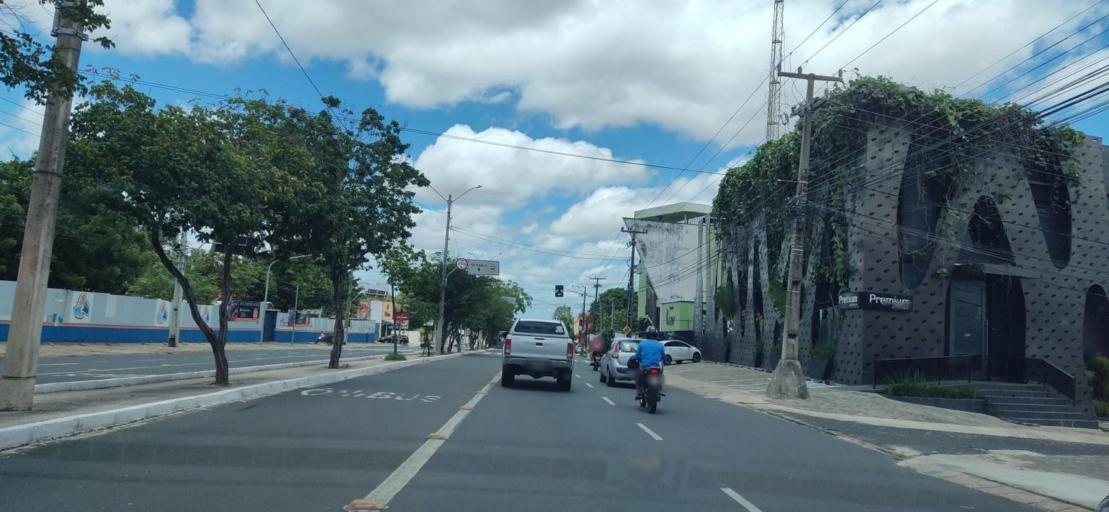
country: BR
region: Piaui
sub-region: Teresina
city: Teresina
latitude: -5.0666
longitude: -42.7705
